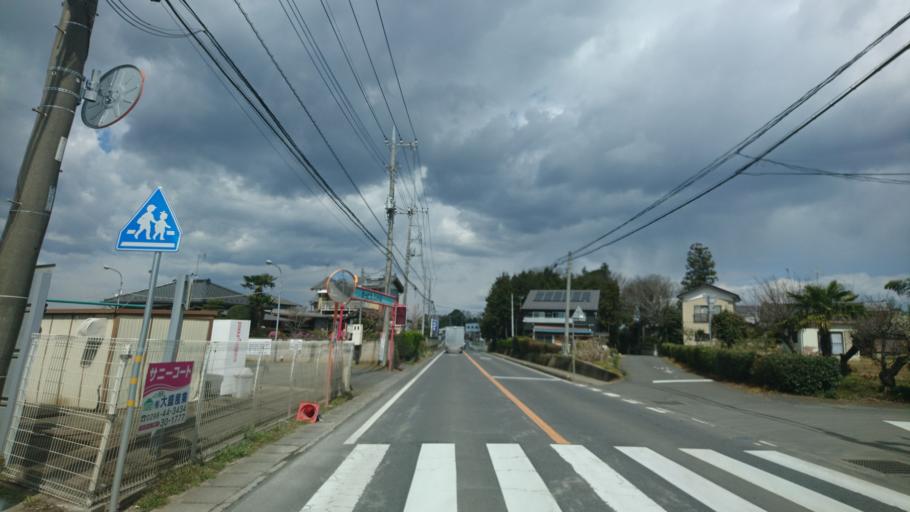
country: JP
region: Ibaraki
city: Yuki
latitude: 36.2259
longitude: 139.9325
